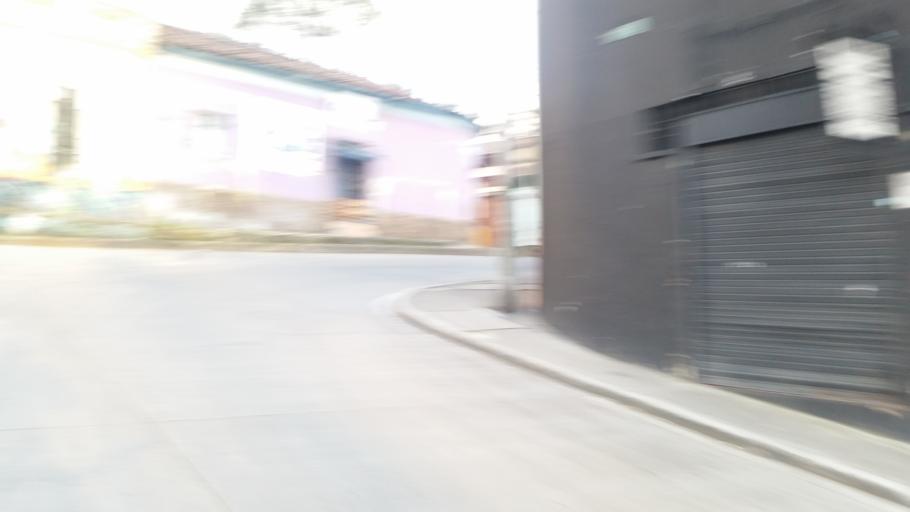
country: CO
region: Bogota D.C.
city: Bogota
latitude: 4.6190
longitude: -74.0662
